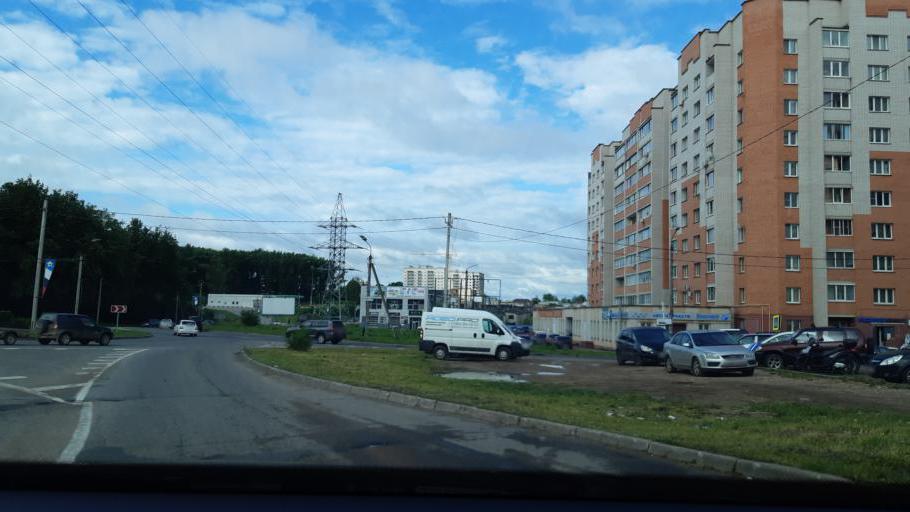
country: RU
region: Smolensk
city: Smolensk
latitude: 54.7613
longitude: 32.0841
